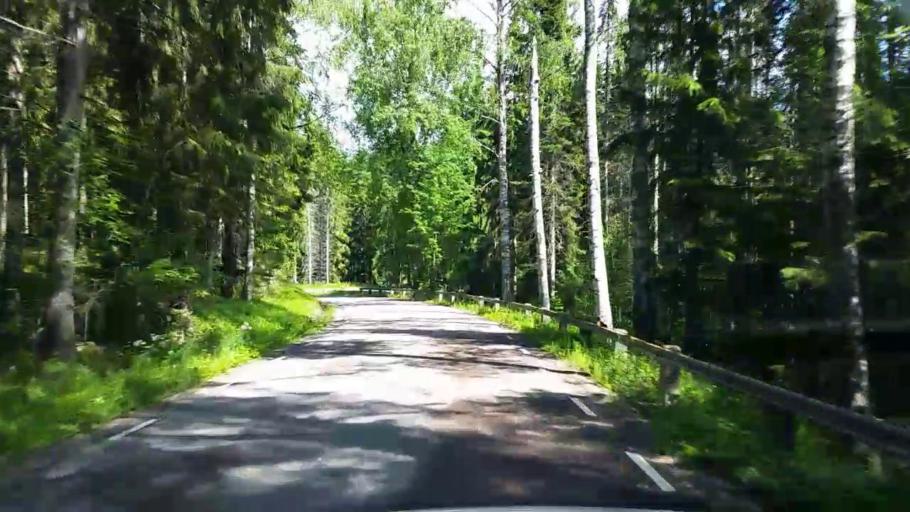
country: SE
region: Vaestmanland
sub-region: Fagersta Kommun
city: Fagersta
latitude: 59.9997
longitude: 15.7585
